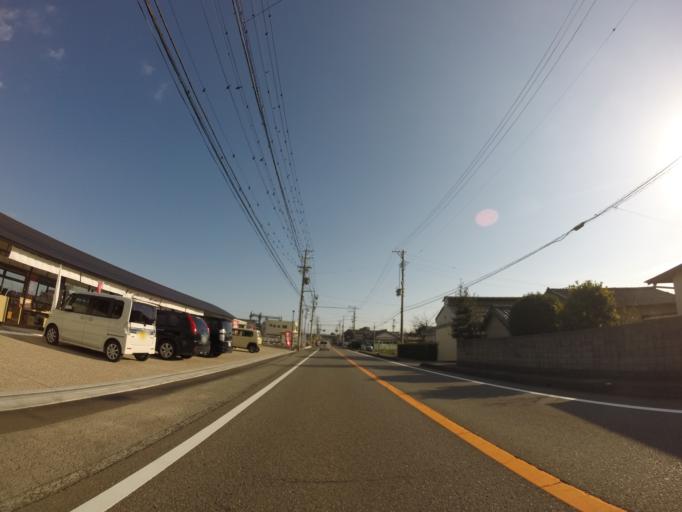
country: JP
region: Shizuoka
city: Shimada
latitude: 34.8139
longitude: 138.2156
